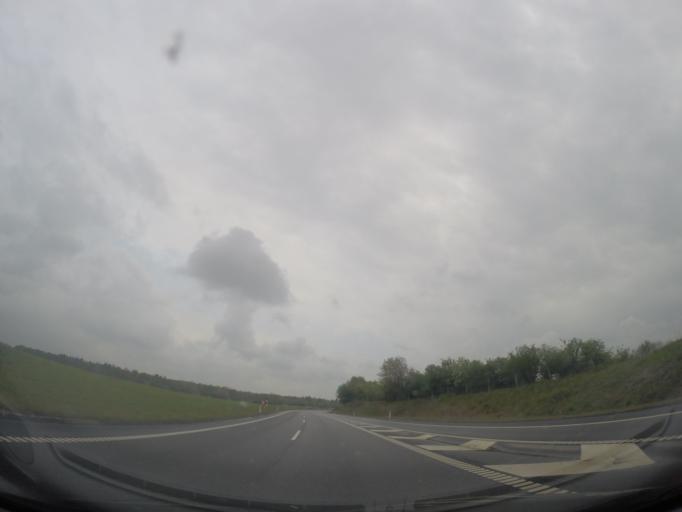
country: DK
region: Capital Region
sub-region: Ballerup Kommune
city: Ballerup
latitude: 55.7026
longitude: 12.3645
